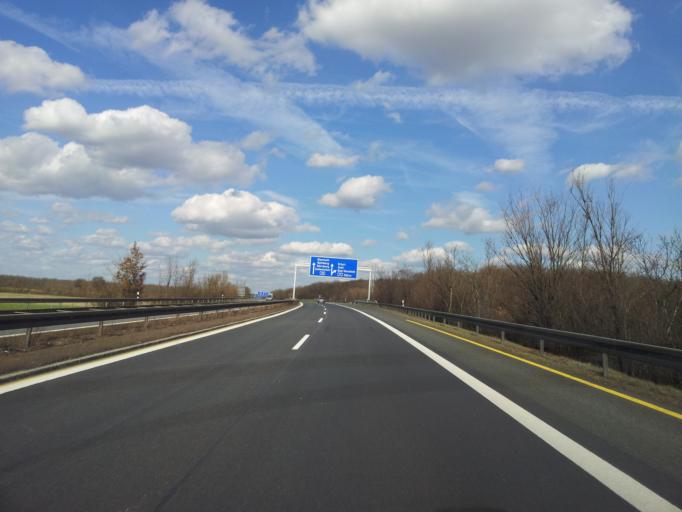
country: DE
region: Bavaria
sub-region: Regierungsbezirk Unterfranken
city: Bergrheinfeld
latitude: 50.0086
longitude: 10.1538
